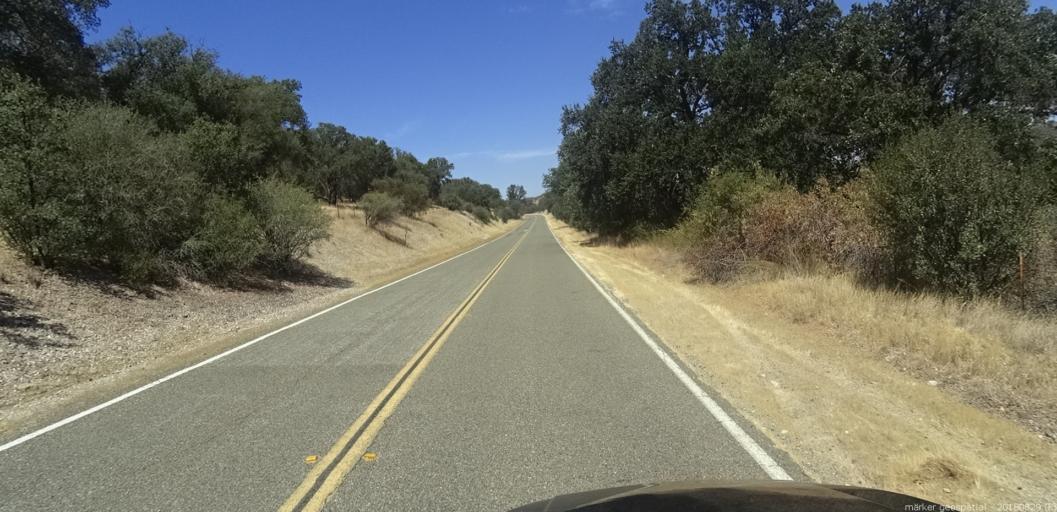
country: US
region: California
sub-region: San Luis Obispo County
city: Lake Nacimiento
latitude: 35.8920
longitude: -121.0821
